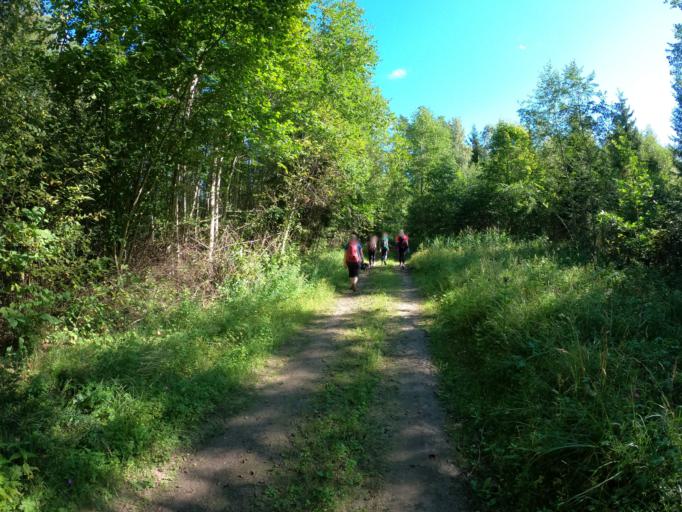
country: LV
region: Talsu Rajons
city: Stende
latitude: 57.0711
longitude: 22.3512
